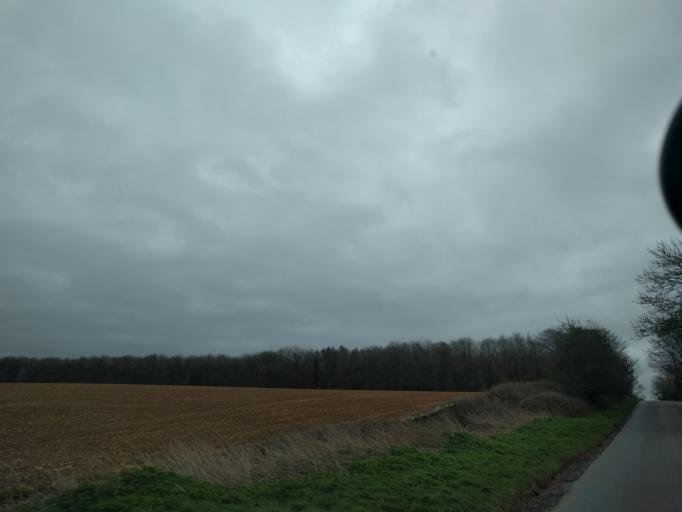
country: GB
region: England
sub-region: Gloucestershire
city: Tetbury
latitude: 51.6239
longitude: -2.2185
